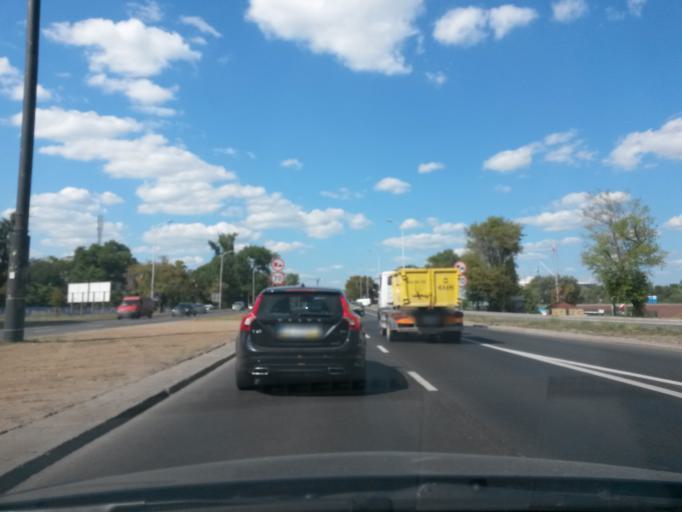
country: PL
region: Masovian Voivodeship
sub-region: Warszawa
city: Srodmiescie
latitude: 52.2260
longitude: 21.0432
